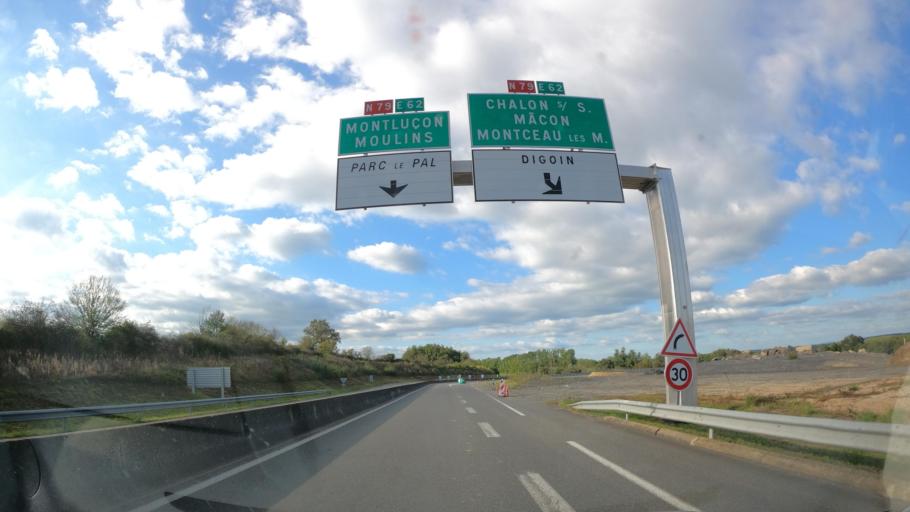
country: FR
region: Auvergne
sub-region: Departement de l'Allier
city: Dompierre-sur-Besbre
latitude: 46.5281
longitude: 3.7197
